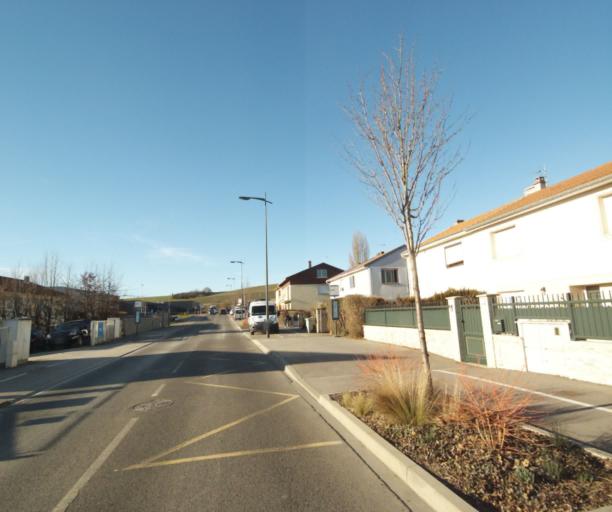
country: FR
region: Lorraine
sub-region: Departement de Meurthe-et-Moselle
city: Seichamps
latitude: 48.7128
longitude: 6.2518
